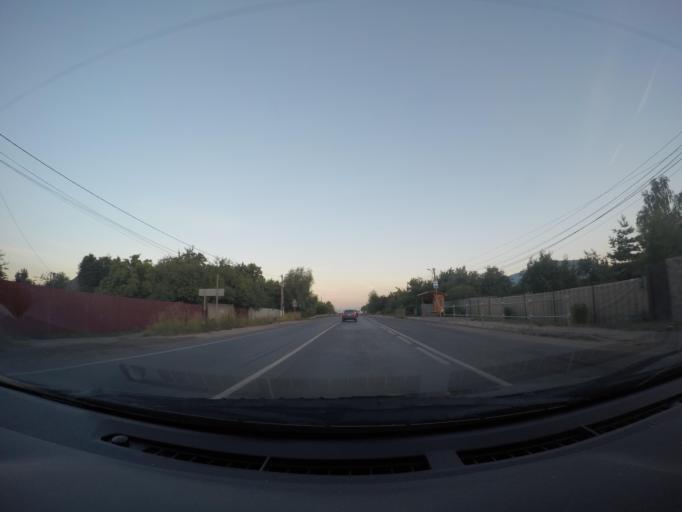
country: RU
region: Moskovskaya
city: Rechitsy
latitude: 55.6029
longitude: 38.4420
